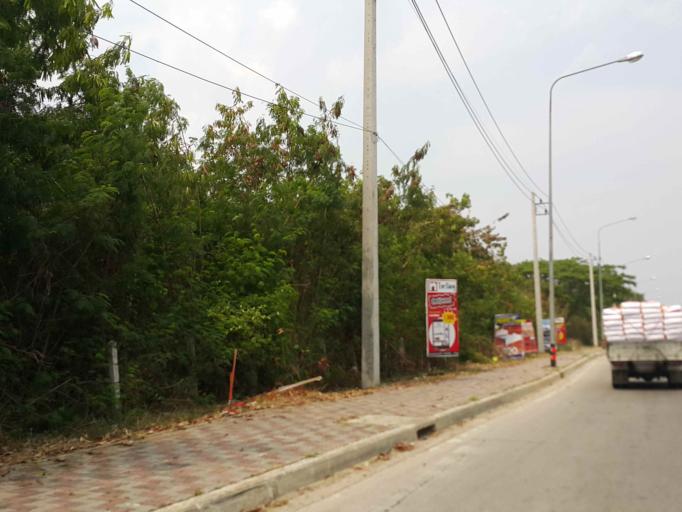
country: TH
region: Chiang Mai
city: Saraphi
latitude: 18.7550
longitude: 99.0362
